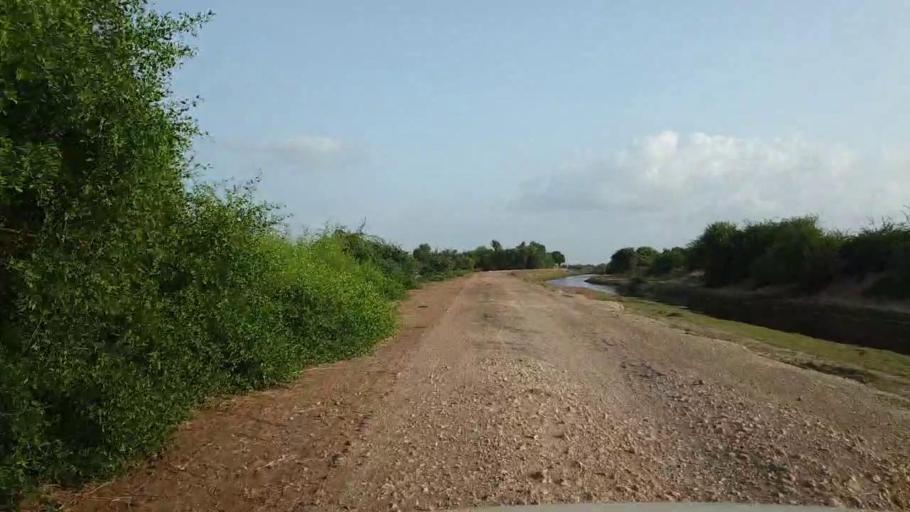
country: PK
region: Sindh
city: Kario
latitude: 24.8385
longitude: 68.6523
